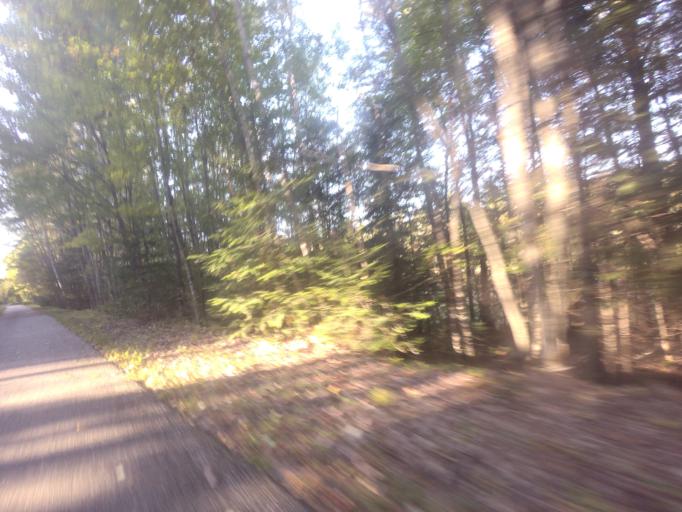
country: CA
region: Quebec
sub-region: Laurentides
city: Riviere-Rouge
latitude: 46.4392
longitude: -74.9028
